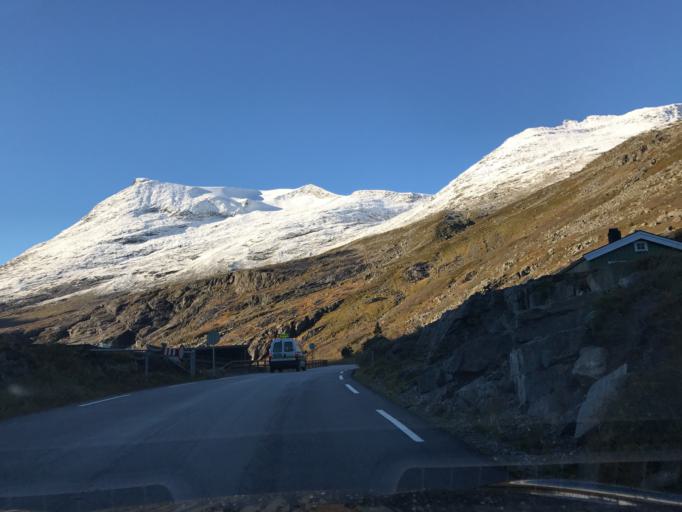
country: NO
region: More og Romsdal
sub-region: Rauma
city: Andalsnes
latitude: 62.4549
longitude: 7.6661
